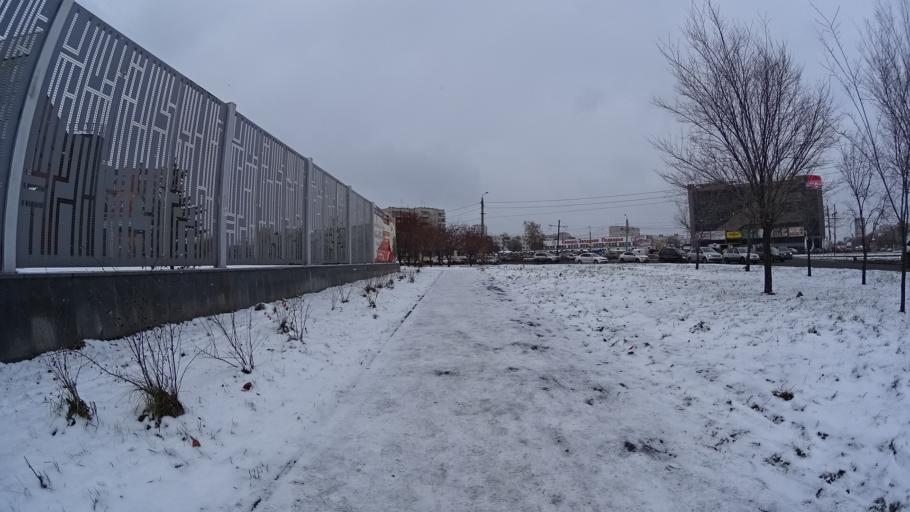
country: RU
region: Chelyabinsk
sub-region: Gorod Chelyabinsk
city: Chelyabinsk
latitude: 55.1884
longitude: 61.3204
